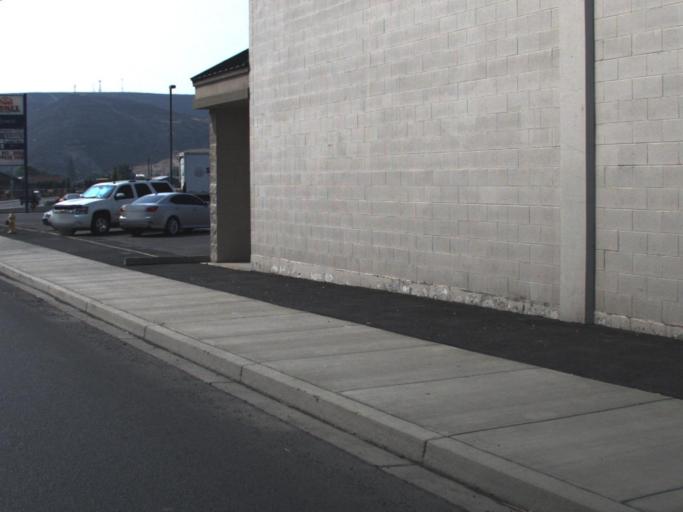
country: US
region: Washington
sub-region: Yakima County
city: Selah
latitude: 46.6511
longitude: -120.5283
